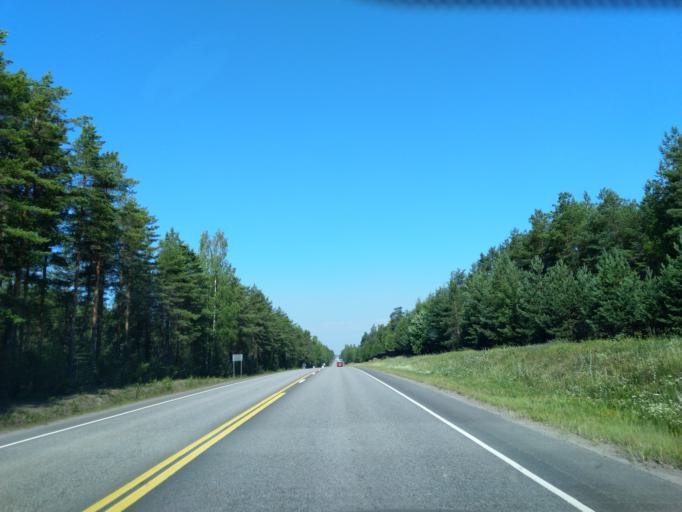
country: FI
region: Satakunta
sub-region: Pori
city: Harjavalta
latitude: 61.2979
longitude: 22.1514
